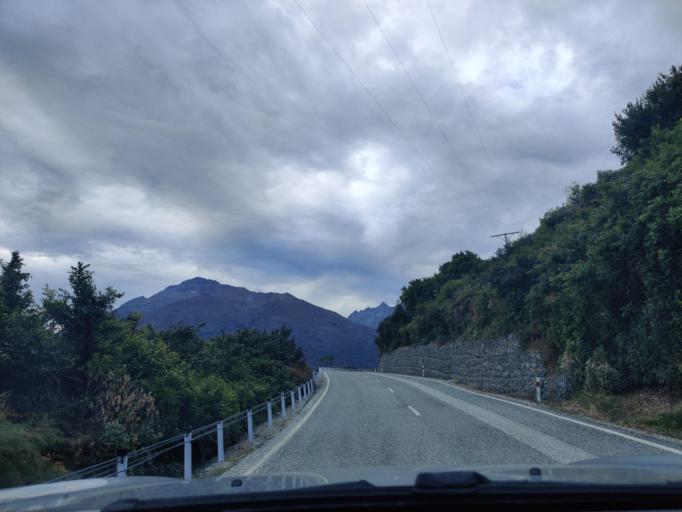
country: NZ
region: Otago
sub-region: Queenstown-Lakes District
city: Wanaka
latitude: -44.3720
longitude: 169.1822
